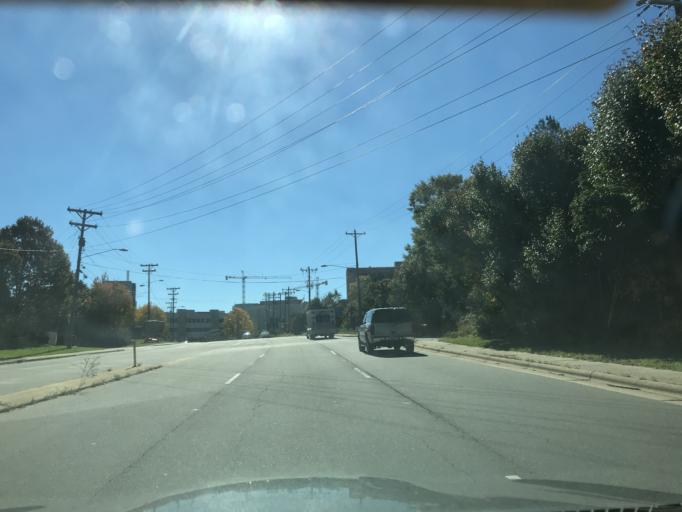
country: US
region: North Carolina
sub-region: Durham County
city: Durham
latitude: 36.0118
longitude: -78.9370
